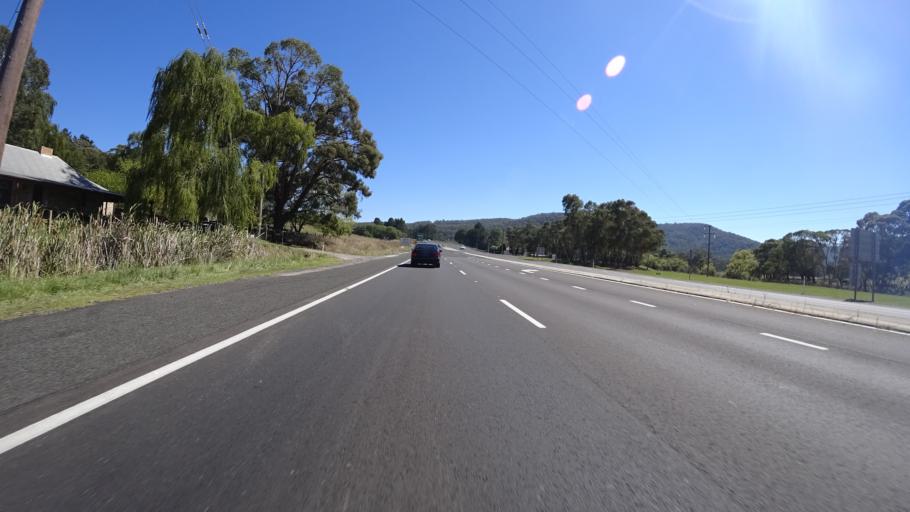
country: AU
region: New South Wales
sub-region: Lithgow
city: Lithgow
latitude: -33.4367
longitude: 150.1130
